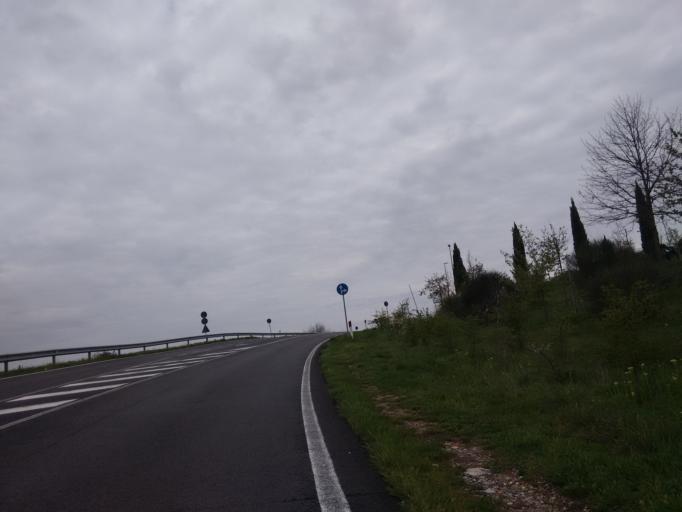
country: IT
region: Tuscany
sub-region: Province of Florence
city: Strada in Chianti
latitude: 43.6540
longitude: 11.3015
